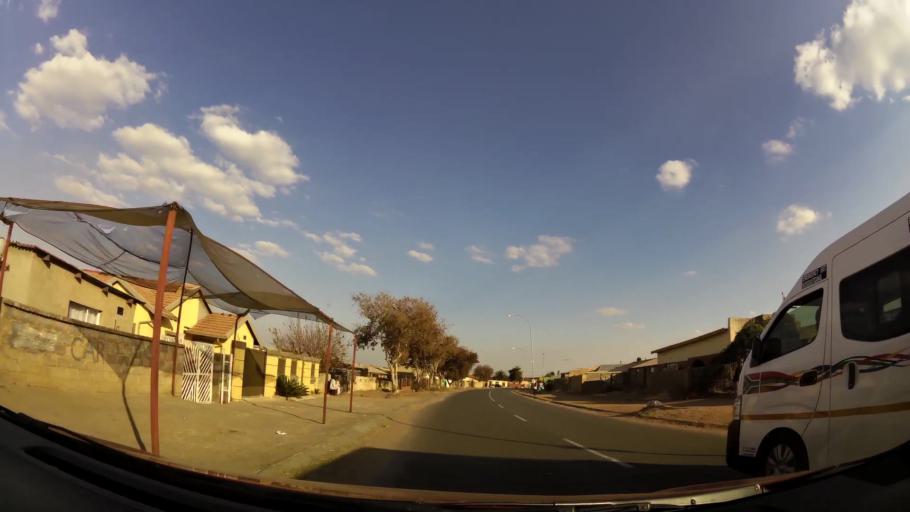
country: ZA
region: Gauteng
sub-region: City of Johannesburg Metropolitan Municipality
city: Soweto
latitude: -26.2337
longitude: 27.9017
